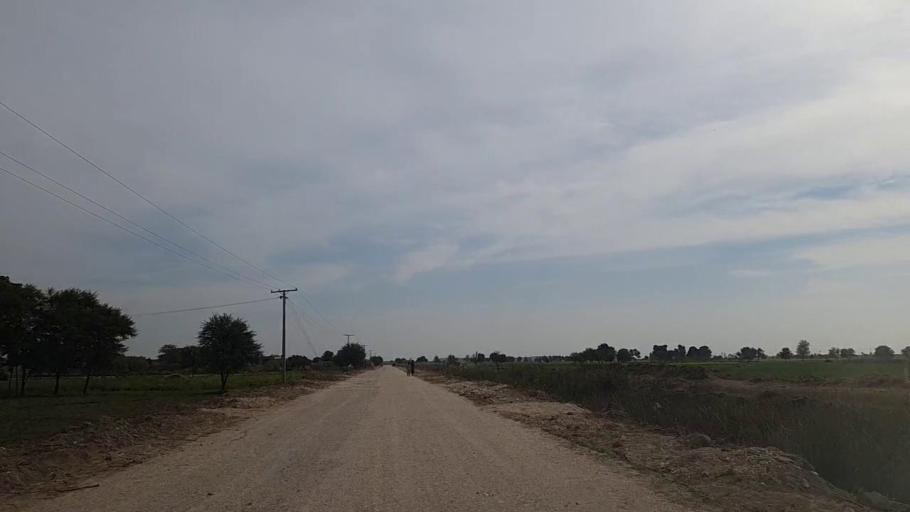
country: PK
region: Sindh
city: Daur
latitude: 26.4144
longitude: 68.4896
